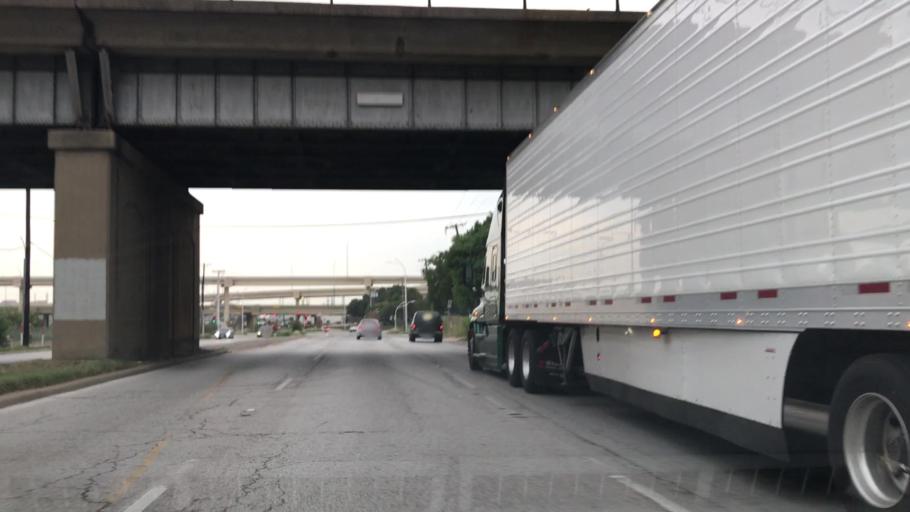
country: US
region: Texas
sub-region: Dallas County
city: Dallas
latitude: 32.7791
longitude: -96.8133
